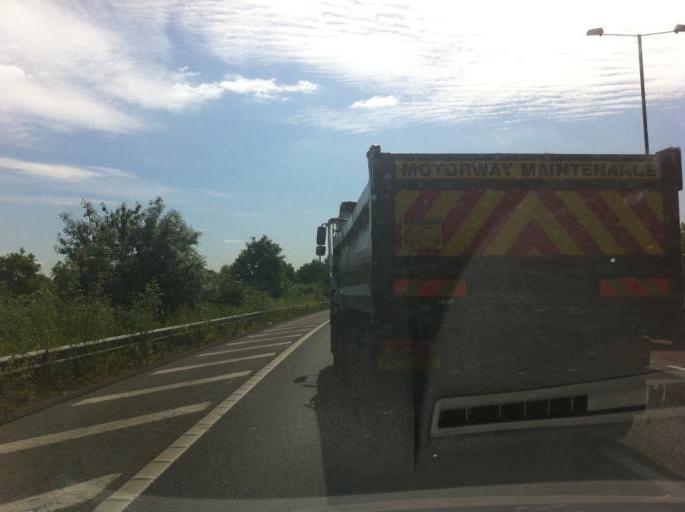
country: GB
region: England
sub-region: Greater London
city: Isleworth
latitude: 51.4957
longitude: -0.3334
